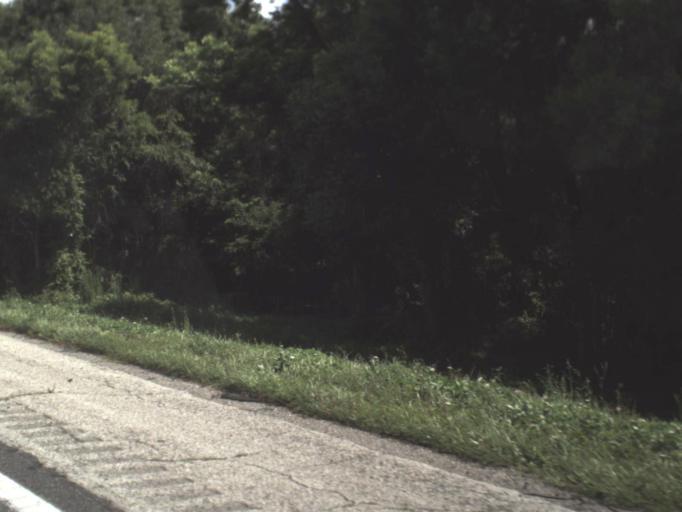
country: US
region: Florida
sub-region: Alachua County
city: Alachua
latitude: 29.7804
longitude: -82.5115
